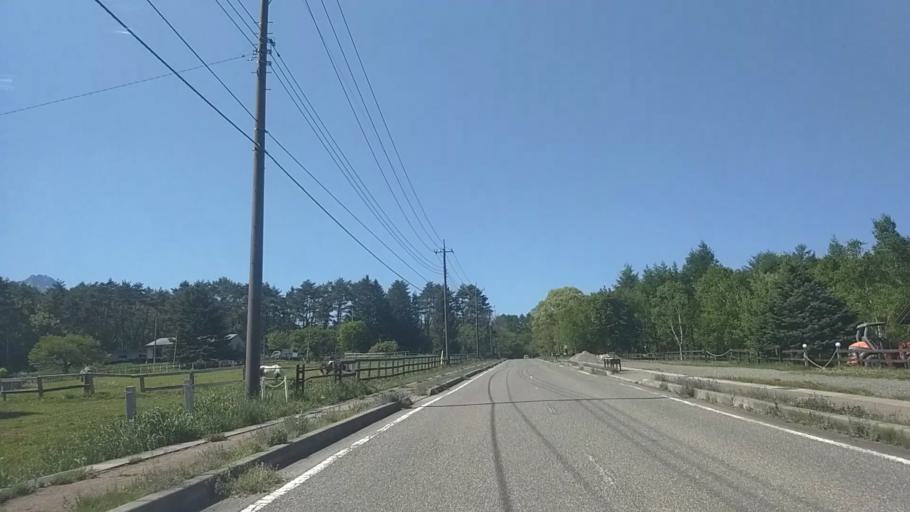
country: JP
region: Yamanashi
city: Nirasaki
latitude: 35.9076
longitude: 138.4323
